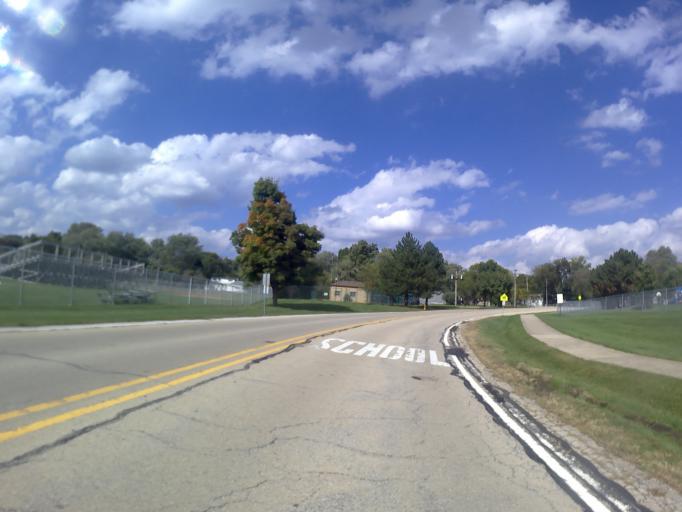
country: US
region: Illinois
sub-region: DuPage County
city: Lisle
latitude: 41.7904
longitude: -88.0680
